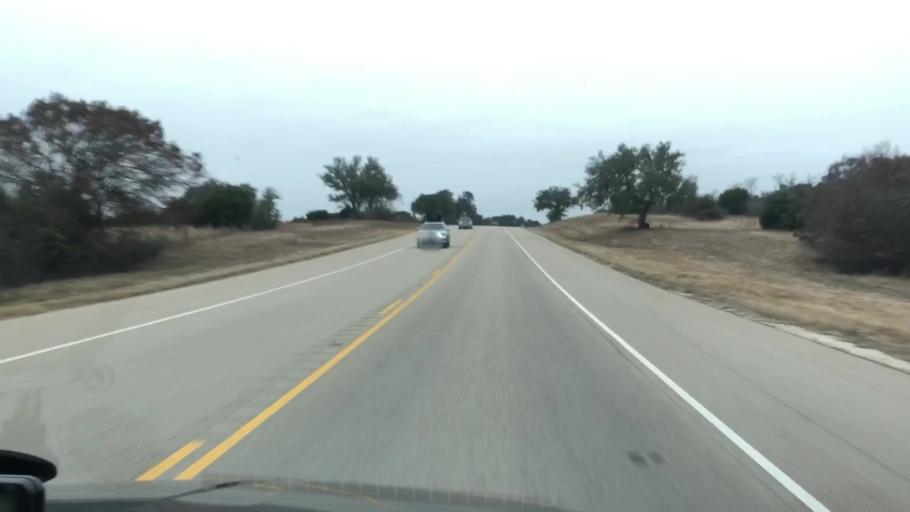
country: US
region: Texas
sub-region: Hamilton County
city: Hamilton
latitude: 31.5432
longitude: -98.1584
